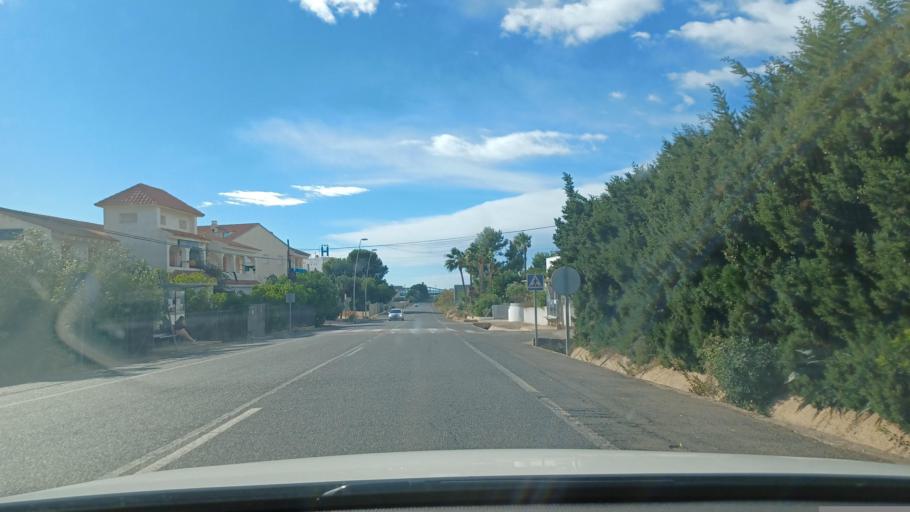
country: ES
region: Catalonia
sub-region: Provincia de Tarragona
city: Sant Carles de la Rapita
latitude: 40.5843
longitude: 0.5568
